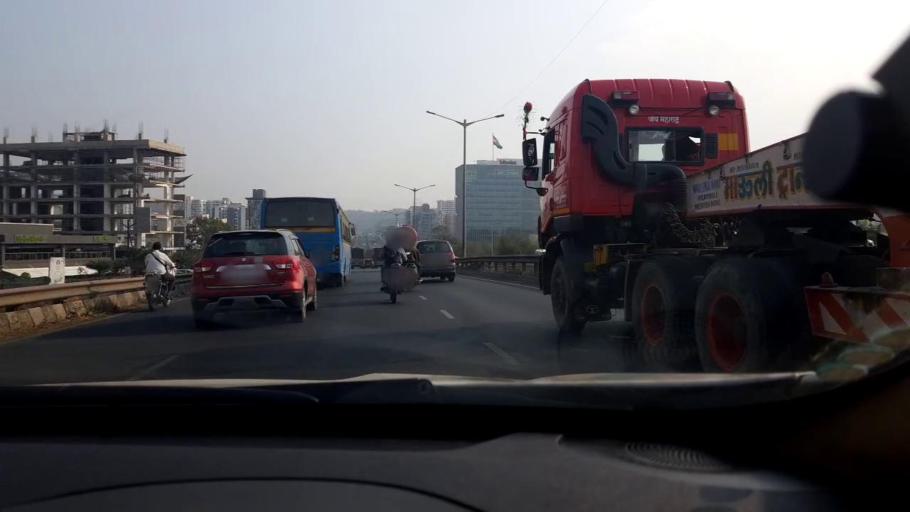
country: IN
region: Maharashtra
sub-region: Pune Division
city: Pimpri
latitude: 18.5608
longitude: 73.7689
